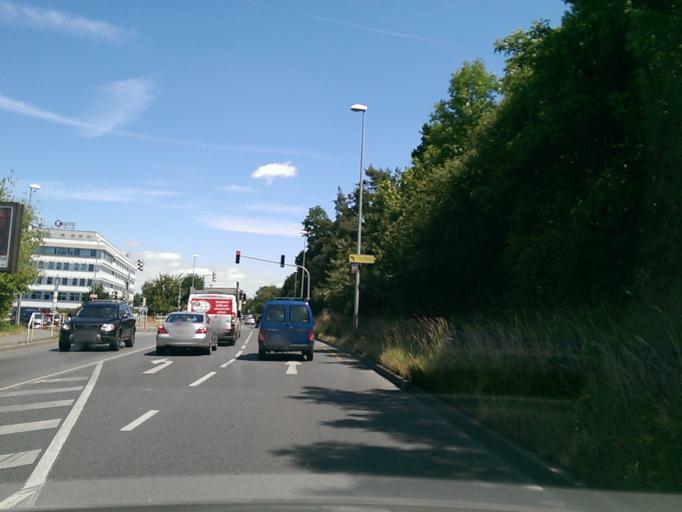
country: CZ
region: Praha
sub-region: Praha 8
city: Liben
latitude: 50.0950
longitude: 14.4751
